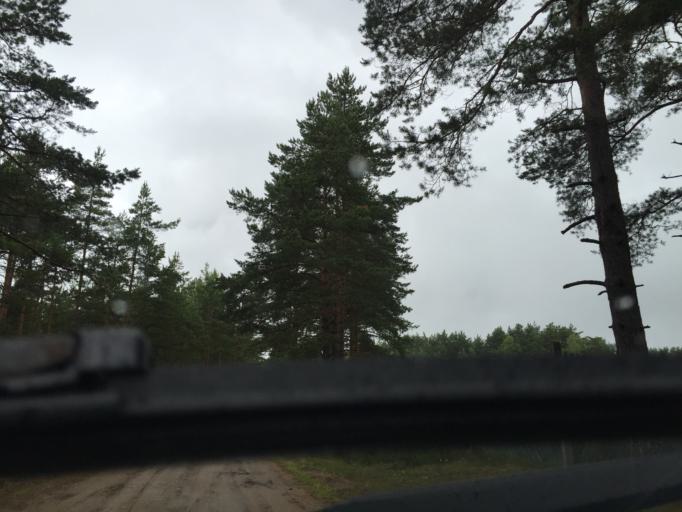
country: LV
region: Riga
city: Jaunciems
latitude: 57.0521
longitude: 24.2051
